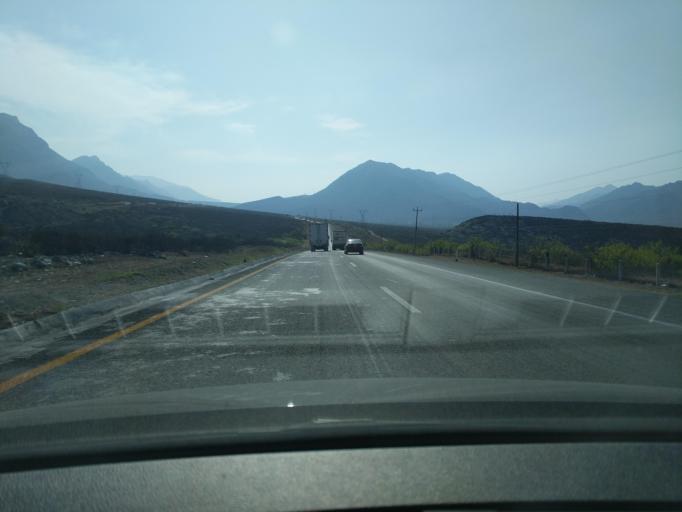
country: MX
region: Nuevo Leon
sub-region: Garcia
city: Las Torres de Guadalupe
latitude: 25.6745
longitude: -100.6853
